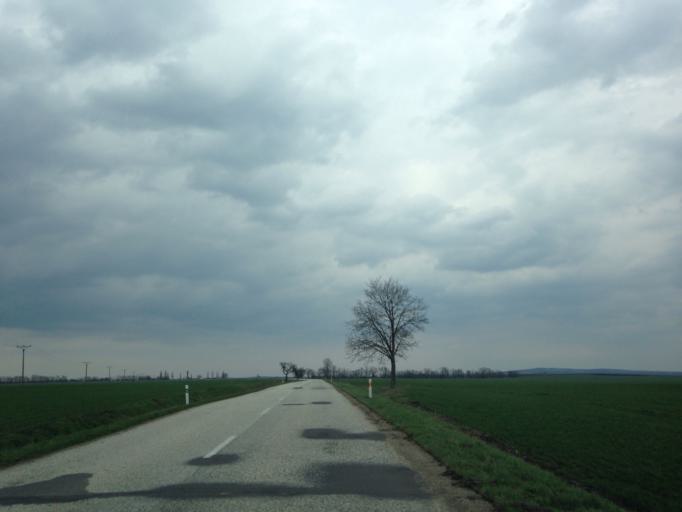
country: SK
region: Nitriansky
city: Svodin
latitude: 47.9835
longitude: 18.3649
